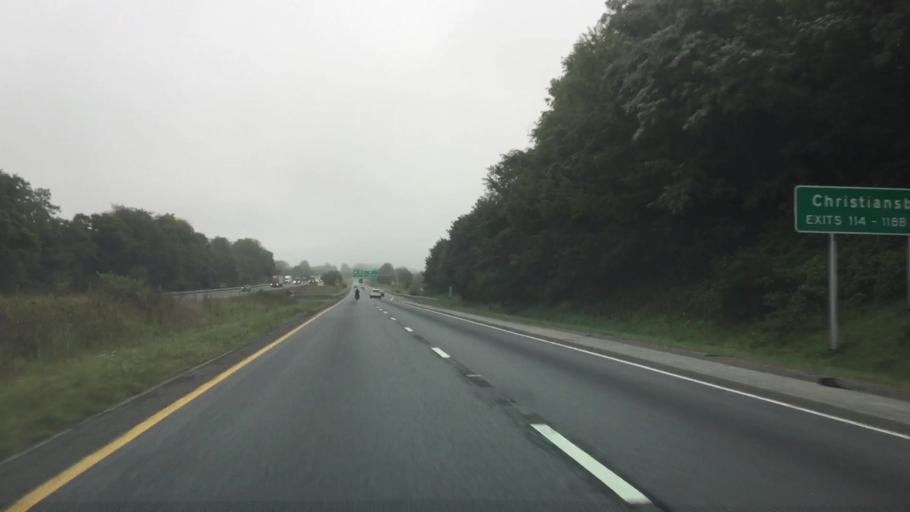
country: US
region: Virginia
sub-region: Montgomery County
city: Christiansburg
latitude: 37.1150
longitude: -80.4303
